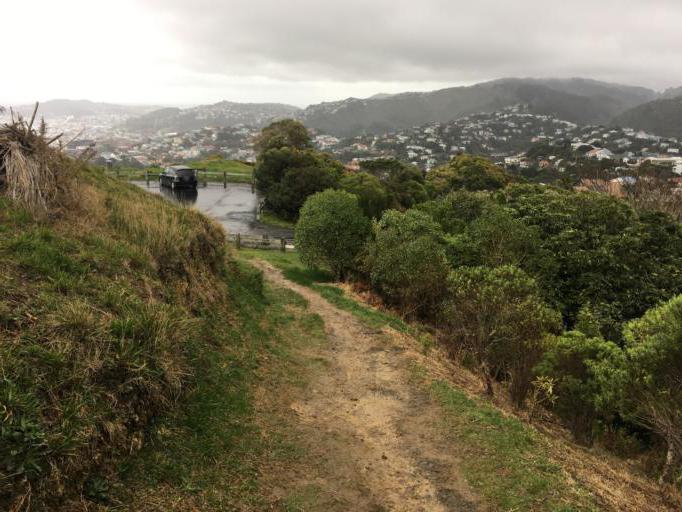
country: NZ
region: Wellington
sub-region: Wellington City
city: Kelburn
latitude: -41.2766
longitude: 174.7639
